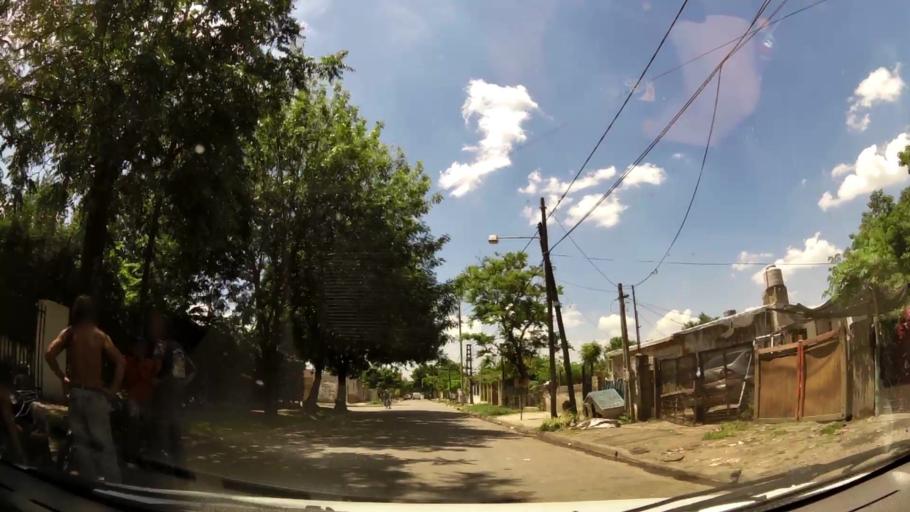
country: AR
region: Buenos Aires
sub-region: Partido de Merlo
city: Merlo
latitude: -34.6453
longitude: -58.6956
